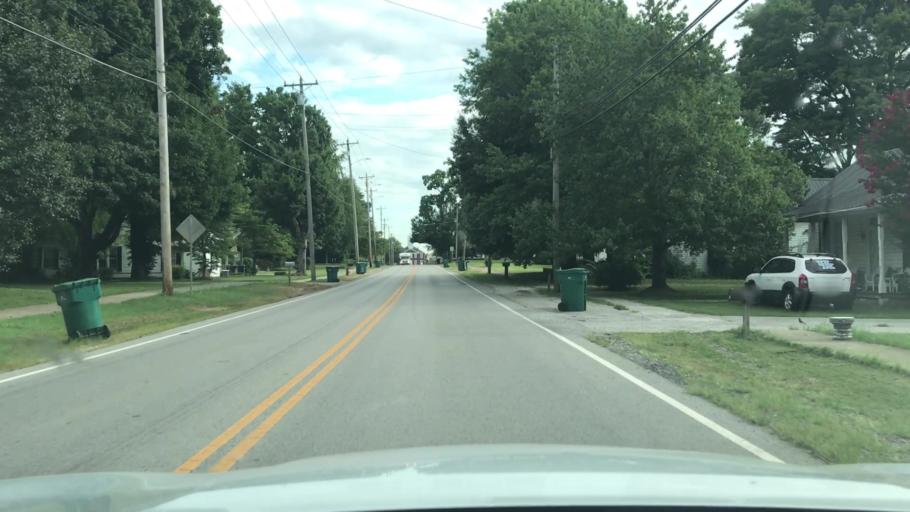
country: US
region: Kentucky
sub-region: Todd County
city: Elkton
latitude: 36.8043
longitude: -87.1556
